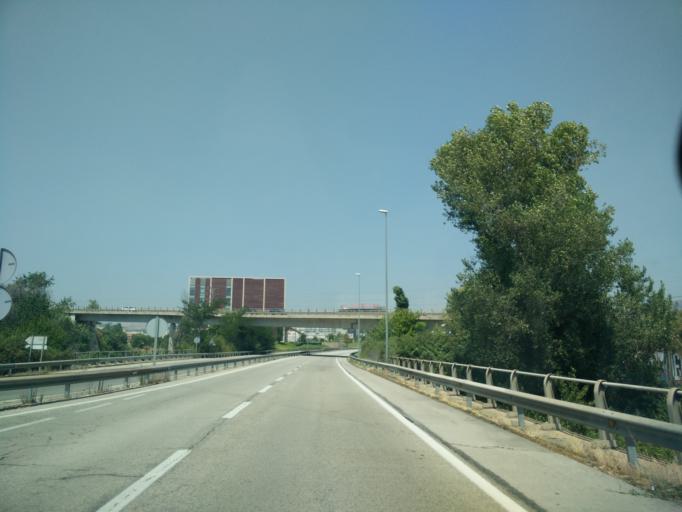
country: ES
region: Catalonia
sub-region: Provincia de Barcelona
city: Terrassa
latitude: 41.5490
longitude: 2.0104
